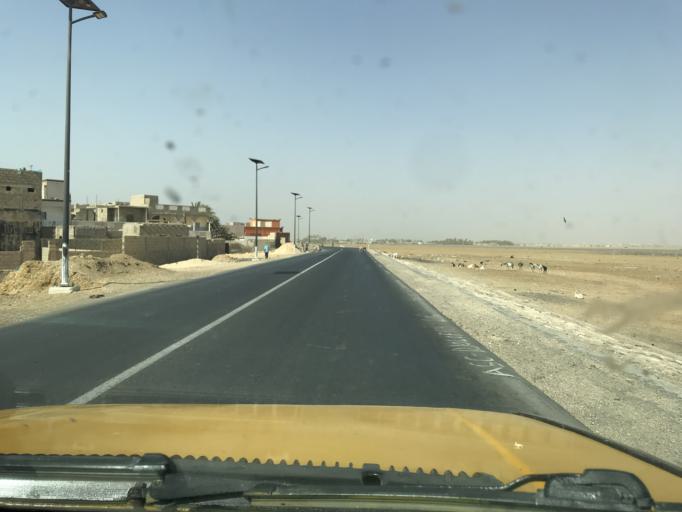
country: SN
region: Saint-Louis
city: Saint-Louis
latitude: 16.0149
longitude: -16.4843
